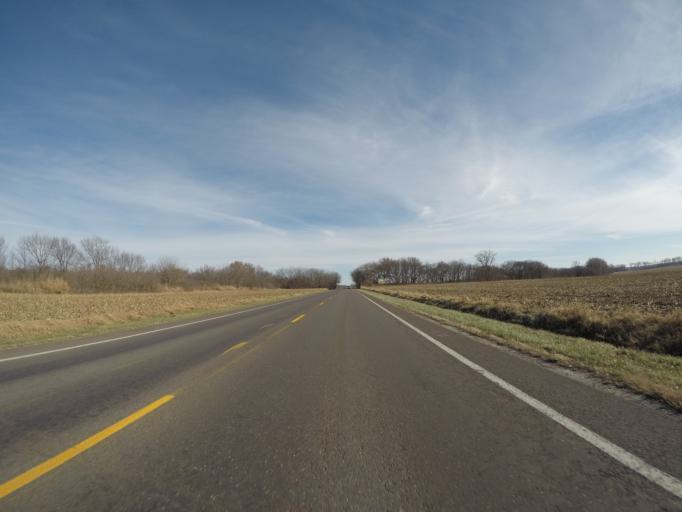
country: US
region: Kansas
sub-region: Pottawatomie County
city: Saint Marys
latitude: 39.2139
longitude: -96.1166
